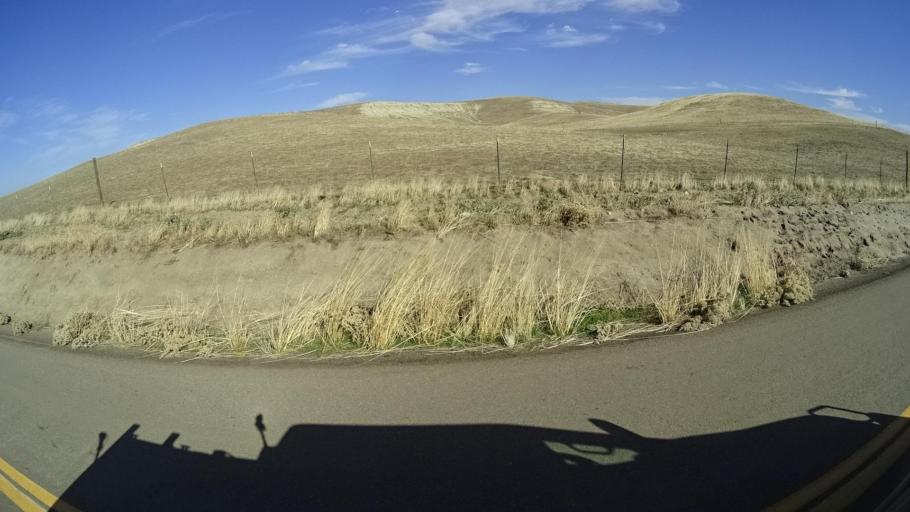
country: US
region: California
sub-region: Kern County
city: Oildale
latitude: 35.6252
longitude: -118.9422
